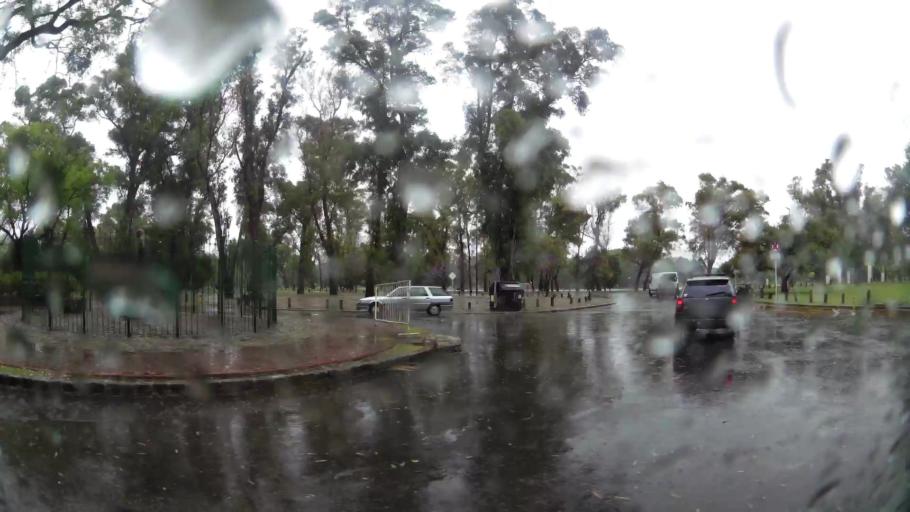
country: AR
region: Buenos Aires F.D.
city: Colegiales
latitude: -34.5615
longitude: -58.4313
